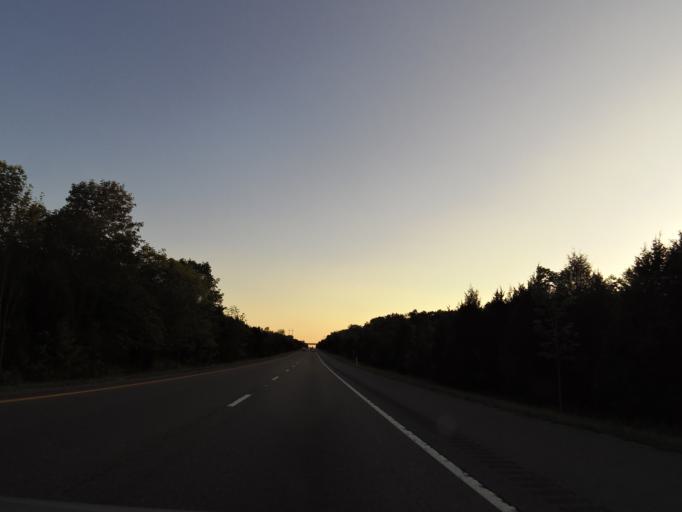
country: US
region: Tennessee
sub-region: Greene County
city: Mosheim
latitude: 36.2646
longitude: -82.9442
